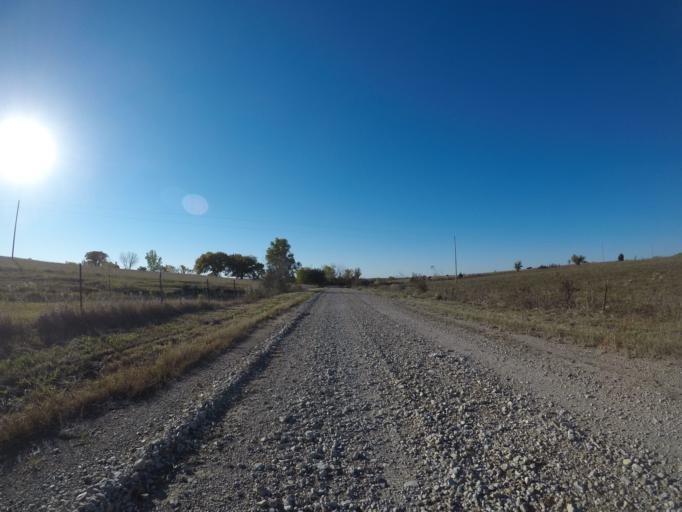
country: US
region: Kansas
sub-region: Wabaunsee County
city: Alma
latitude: 38.9285
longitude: -96.4642
